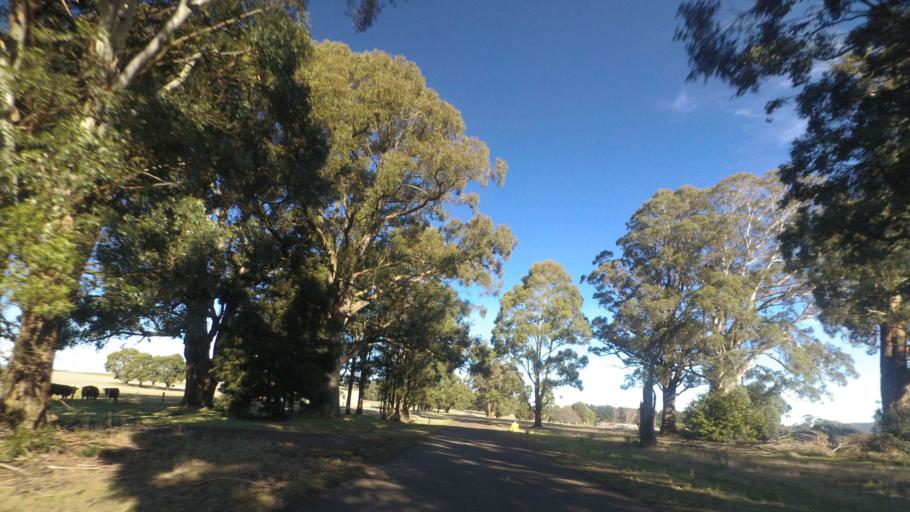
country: AU
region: Victoria
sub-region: Mount Alexander
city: Castlemaine
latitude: -37.3529
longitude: 144.2902
